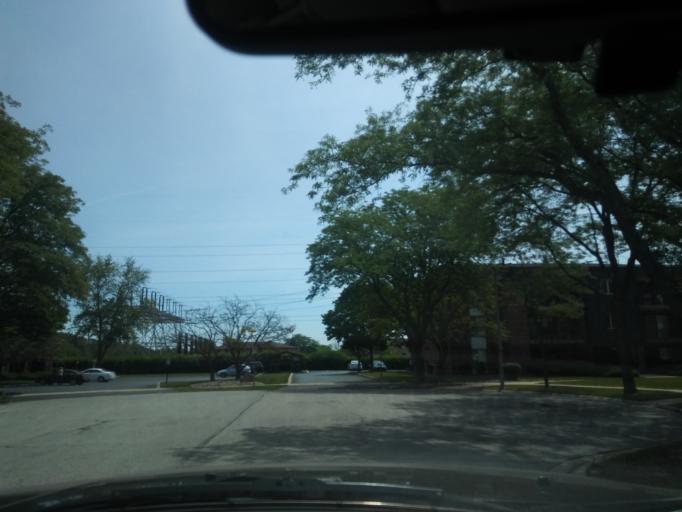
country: US
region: Illinois
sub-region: Cook County
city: Tinley Park
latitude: 41.6162
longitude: -87.8005
